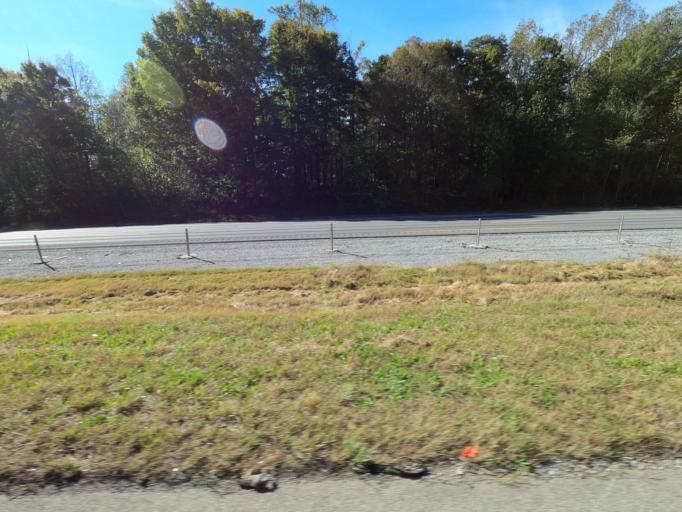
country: US
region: Tennessee
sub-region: Williamson County
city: Fairview
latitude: 36.0253
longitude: -87.1936
